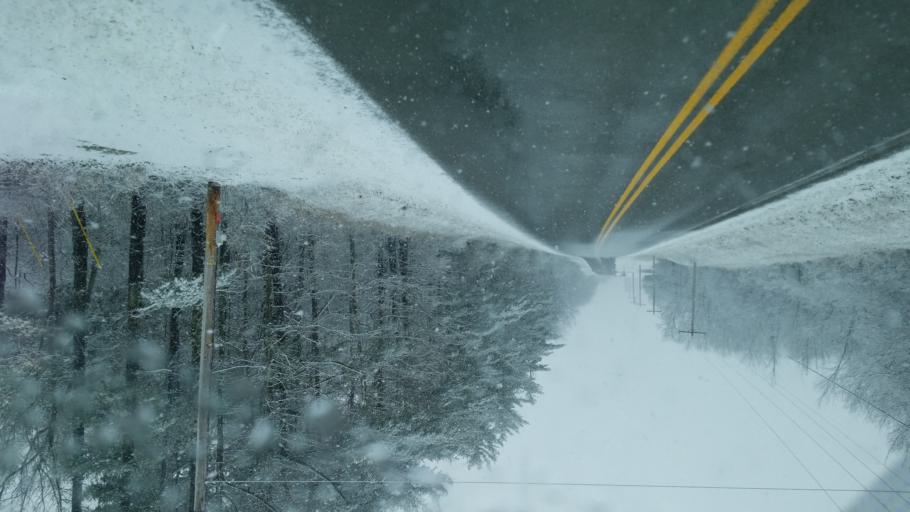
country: US
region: Ohio
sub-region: Logan County
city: Bellefontaine
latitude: 40.3400
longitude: -83.6391
